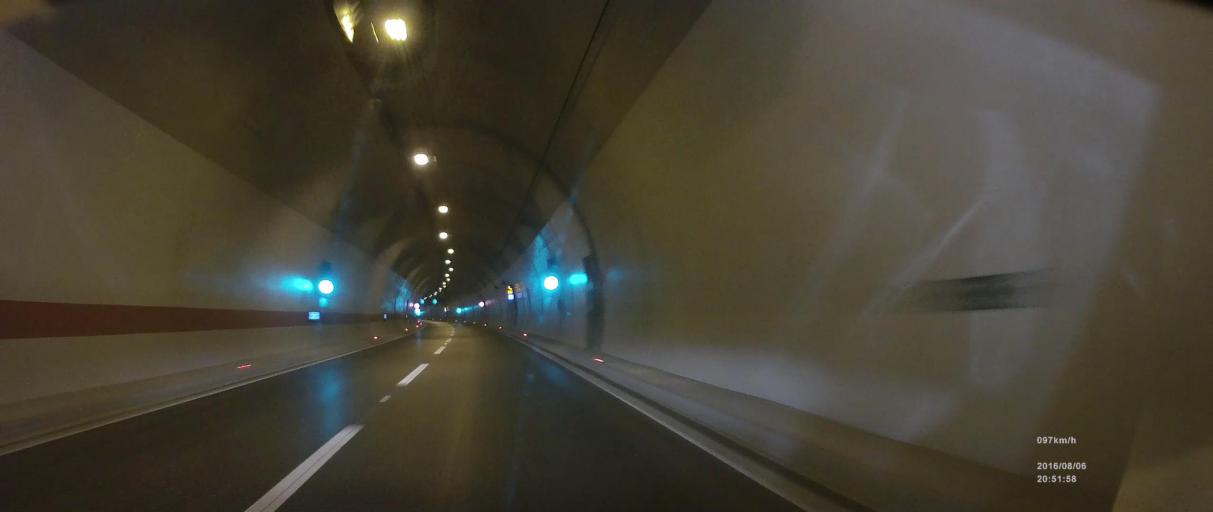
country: BA
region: Federation of Bosnia and Herzegovina
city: Ljubuski
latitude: 43.1223
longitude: 17.4850
